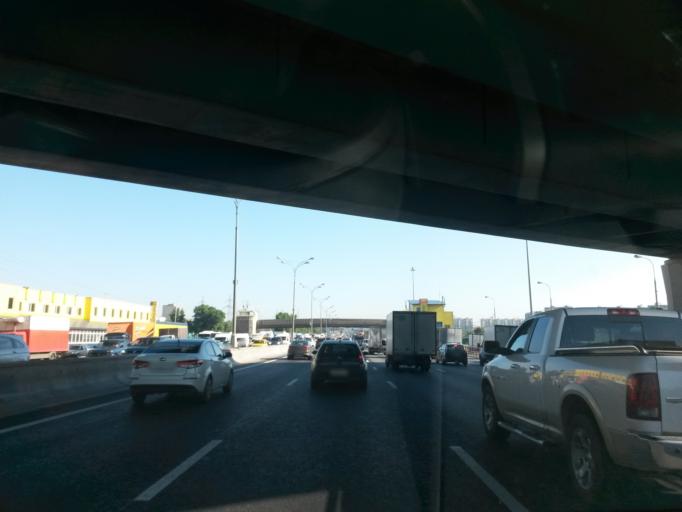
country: RU
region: Moskovskaya
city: Kuskovo
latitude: 55.7306
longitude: 37.8406
